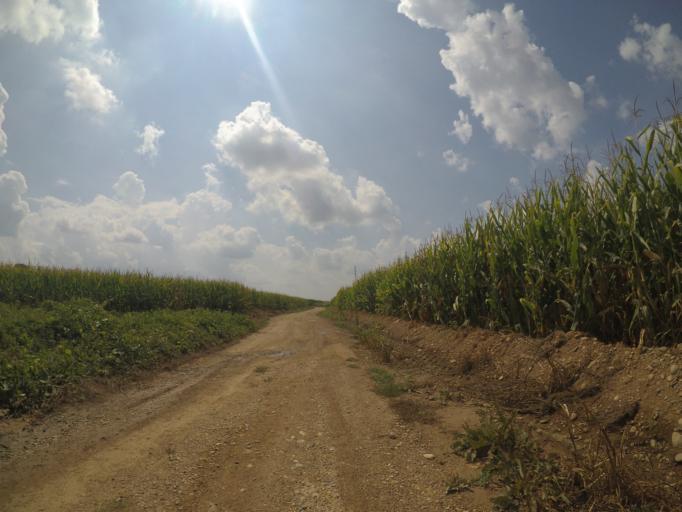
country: IT
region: Friuli Venezia Giulia
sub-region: Provincia di Udine
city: Bertiolo
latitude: 45.9585
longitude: 13.0498
